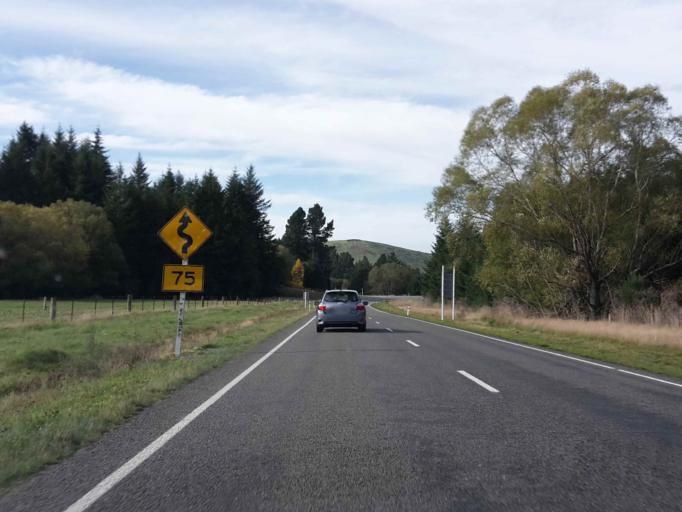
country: NZ
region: Canterbury
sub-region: Timaru District
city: Pleasant Point
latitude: -44.0330
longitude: 170.7028
